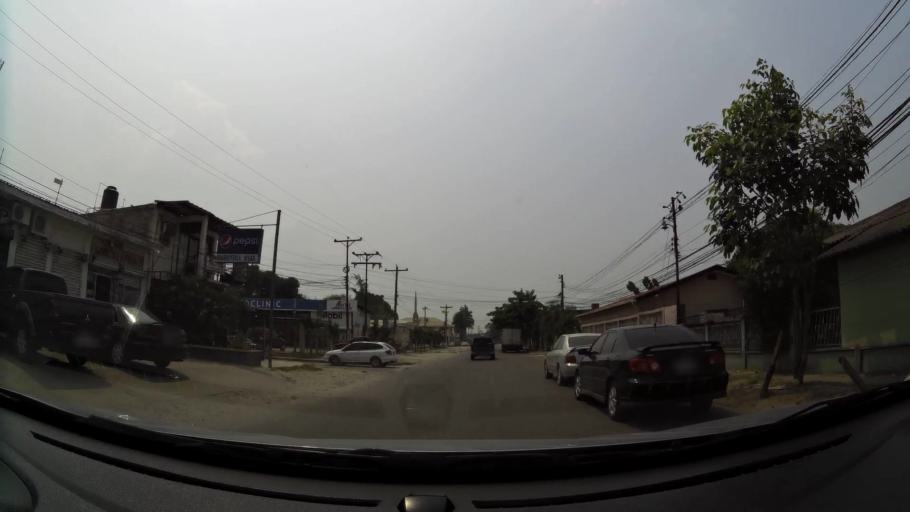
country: HN
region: Cortes
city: La Lima
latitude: 15.4400
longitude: -87.9265
